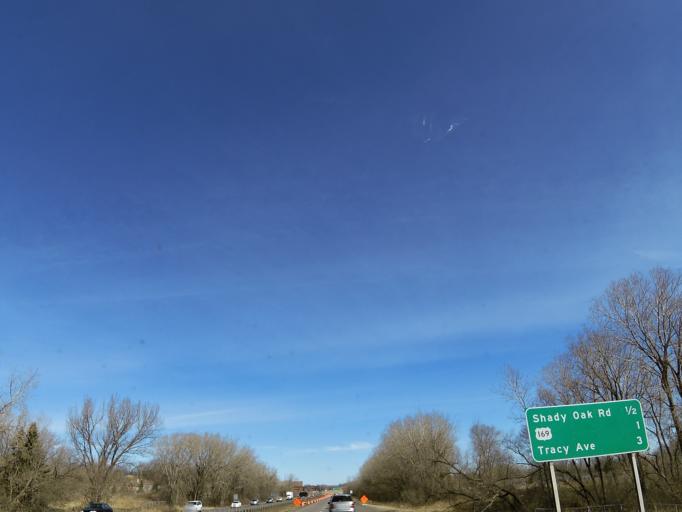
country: US
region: Minnesota
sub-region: Hennepin County
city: Eden Prairie
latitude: 44.8725
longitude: -93.4156
